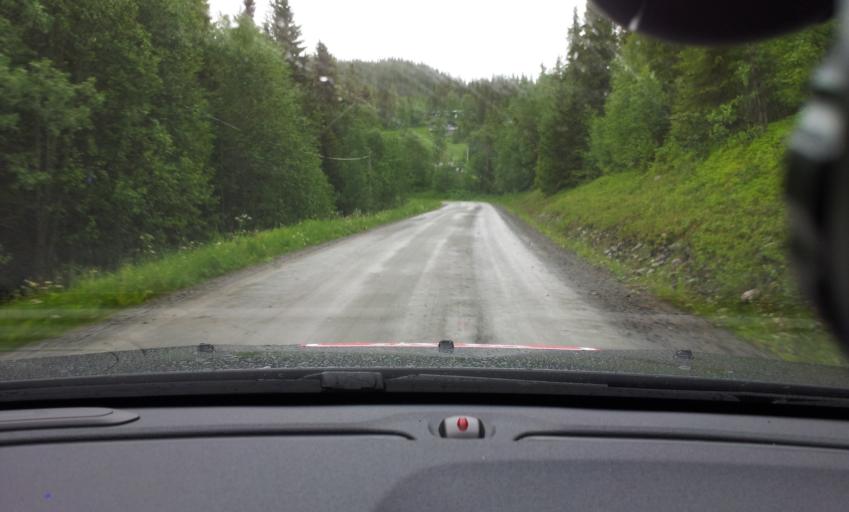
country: SE
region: Jaemtland
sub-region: Are Kommun
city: Are
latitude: 63.4580
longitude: 12.8163
